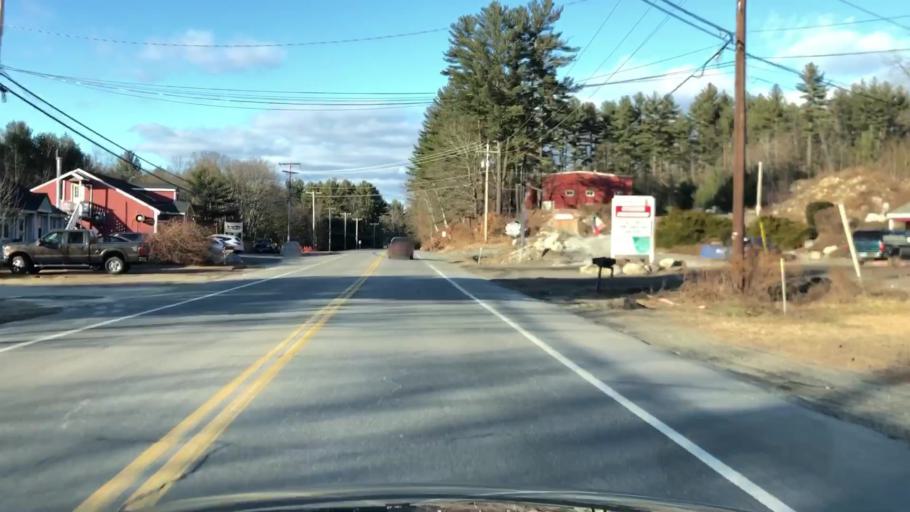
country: US
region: New Hampshire
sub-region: Hillsborough County
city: Brookline
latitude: 42.7558
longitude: -71.6736
